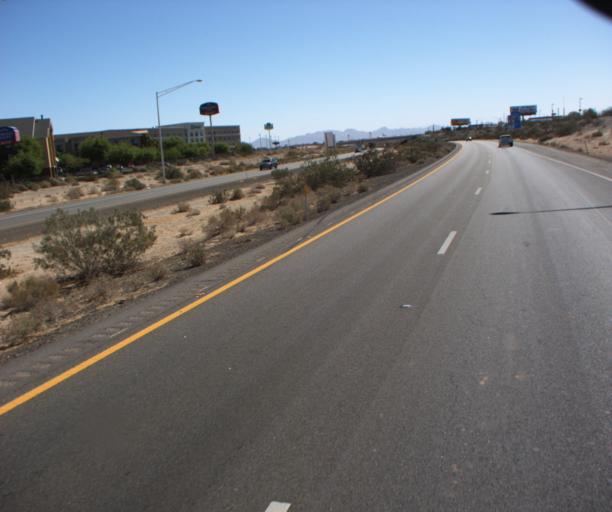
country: US
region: Arizona
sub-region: Yuma County
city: Yuma
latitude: 32.6942
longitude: -114.6040
